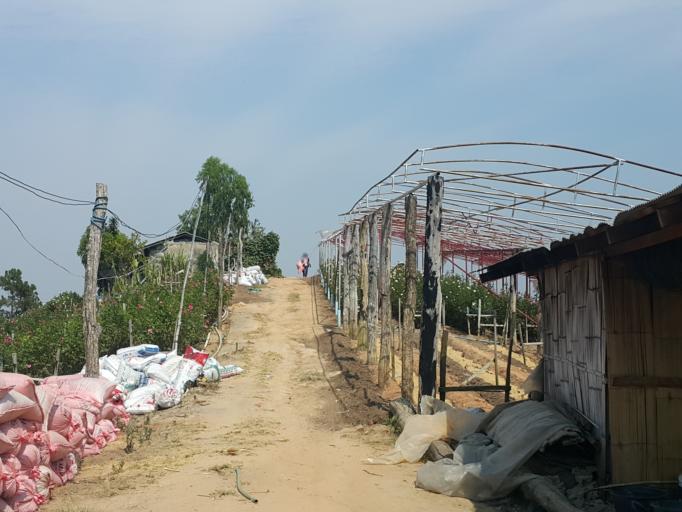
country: TH
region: Chiang Mai
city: Samoeng
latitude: 18.8833
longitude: 98.7971
